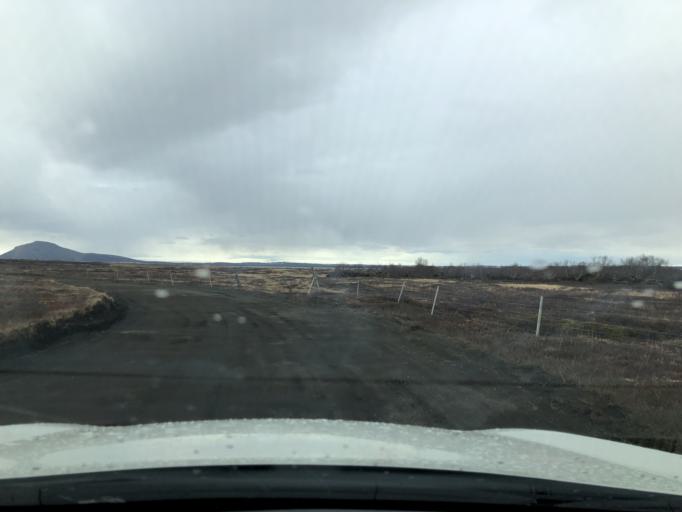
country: IS
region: Northeast
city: Laugar
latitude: 65.6094
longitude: -16.9049
